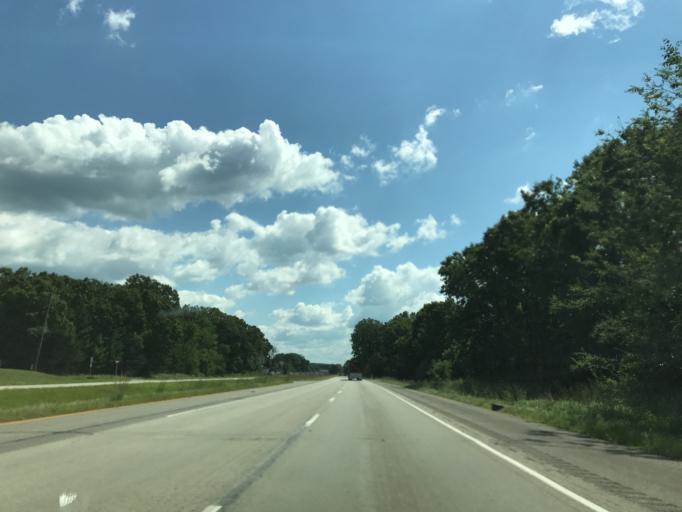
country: US
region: Indiana
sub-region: Starke County
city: Koontz Lake
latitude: 41.3664
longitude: -86.4777
